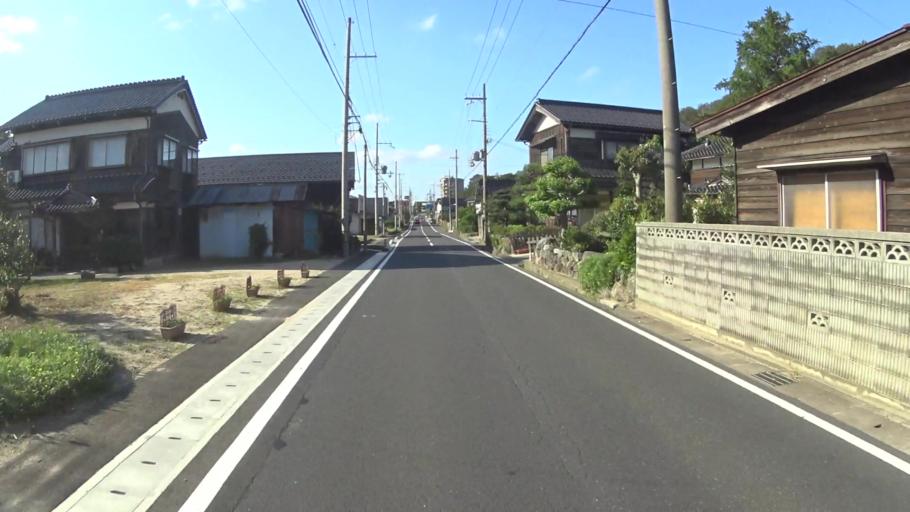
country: JP
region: Hyogo
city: Toyooka
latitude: 35.6545
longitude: 134.9693
